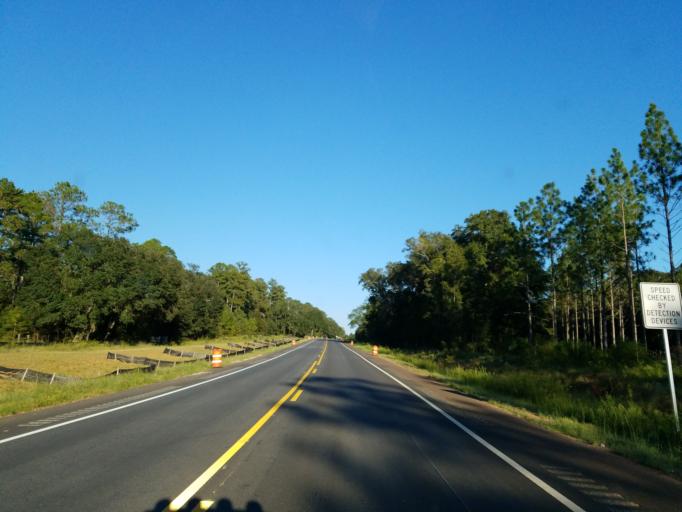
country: US
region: Georgia
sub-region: Lee County
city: Leesburg
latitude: 31.7249
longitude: -84.0154
